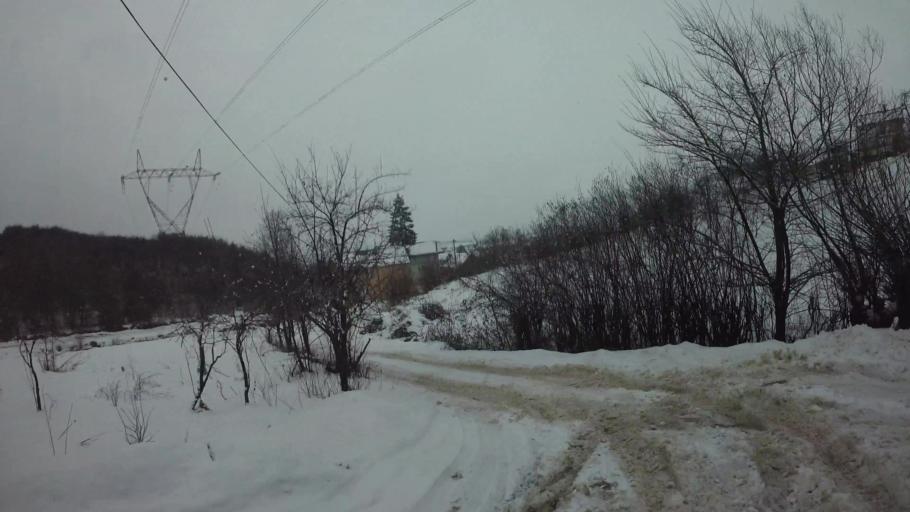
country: BA
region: Federation of Bosnia and Herzegovina
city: Hadzici
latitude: 43.8547
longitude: 18.2700
